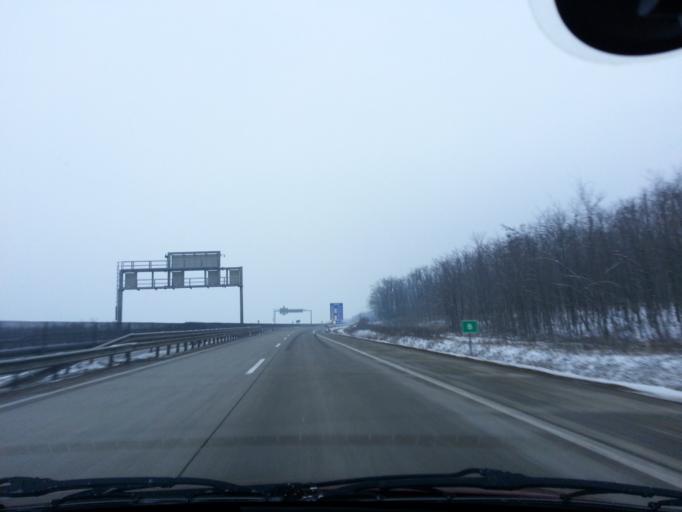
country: HU
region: Pest
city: Godollo
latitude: 47.5798
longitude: 19.3187
